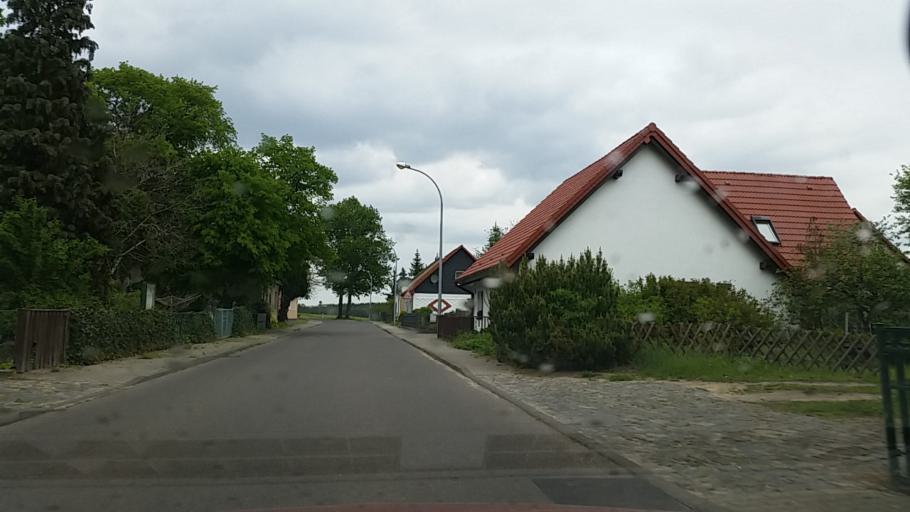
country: DE
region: Brandenburg
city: Rauen
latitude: 52.3141
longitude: 13.9643
